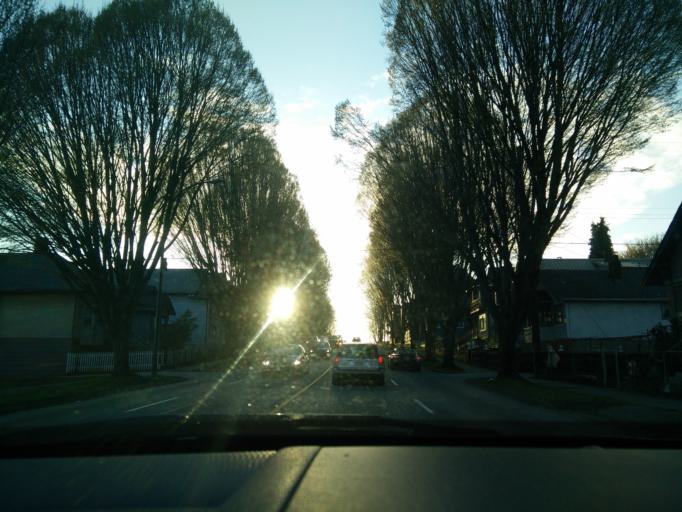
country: CA
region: British Columbia
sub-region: Fraser Valley Regional District
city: North Vancouver
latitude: 49.2696
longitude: -123.0660
